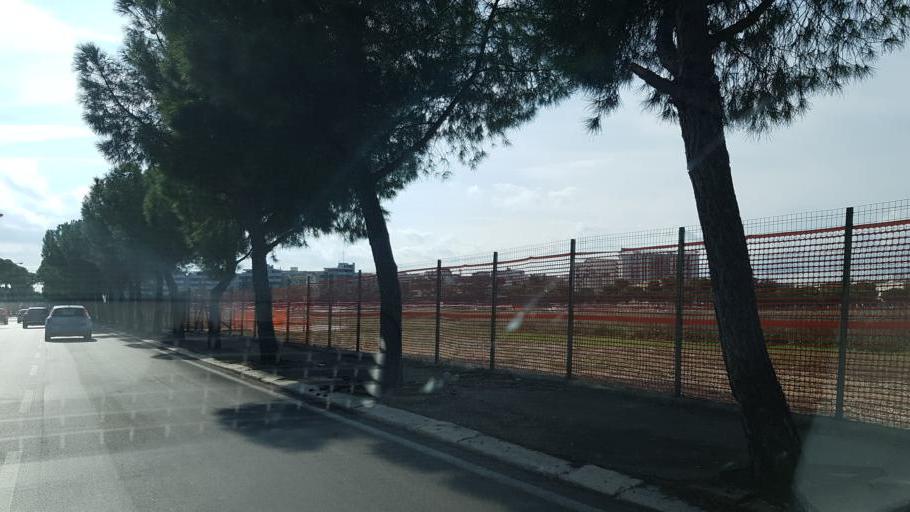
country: IT
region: Apulia
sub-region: Provincia di Foggia
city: Foggia
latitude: 41.4591
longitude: 15.5643
